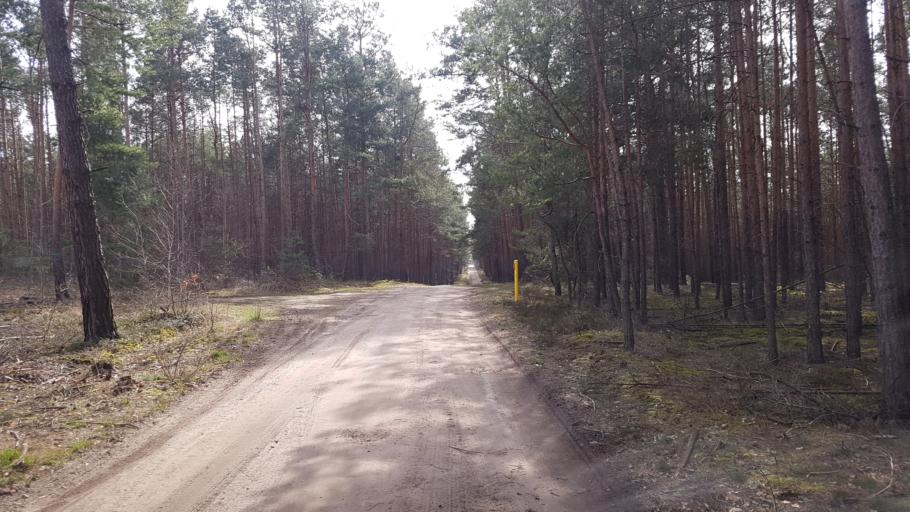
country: DE
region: Brandenburg
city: Doberlug-Kirchhain
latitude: 51.6250
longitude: 13.6057
